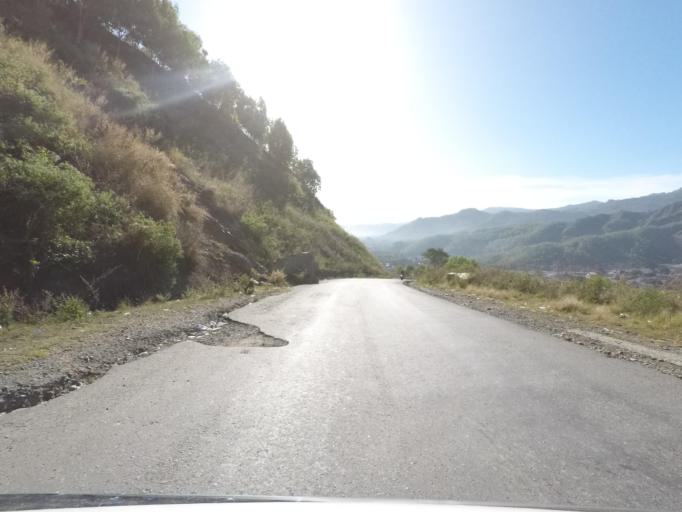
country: TL
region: Dili
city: Dili
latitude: -8.5602
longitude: 125.6395
